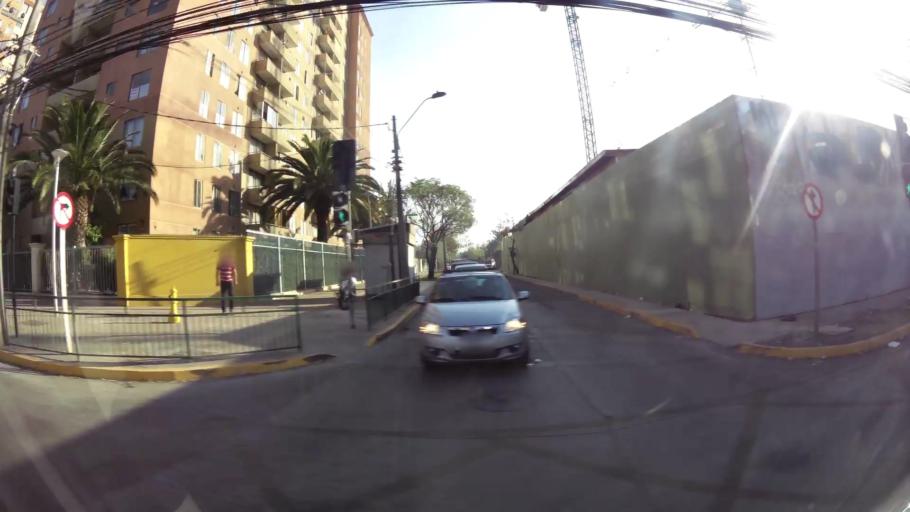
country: CL
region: Santiago Metropolitan
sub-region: Provincia de Santiago
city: Villa Presidente Frei, Nunoa, Santiago, Chile
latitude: -33.5134
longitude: -70.6090
